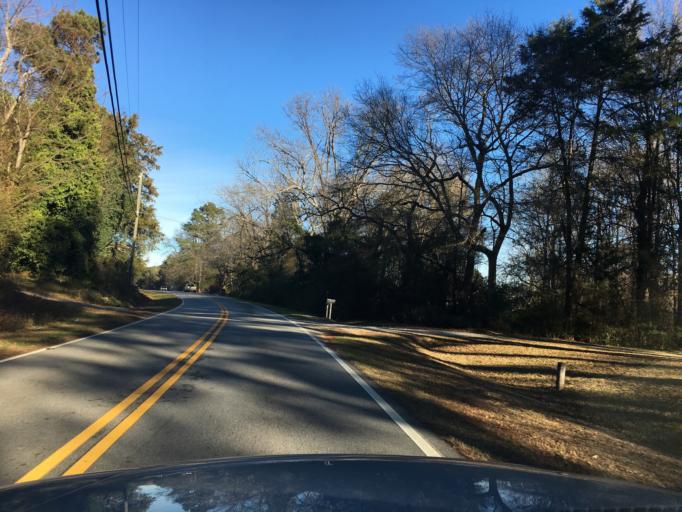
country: US
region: Georgia
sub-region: Rockdale County
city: Conyers
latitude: 33.6612
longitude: -84.0455
